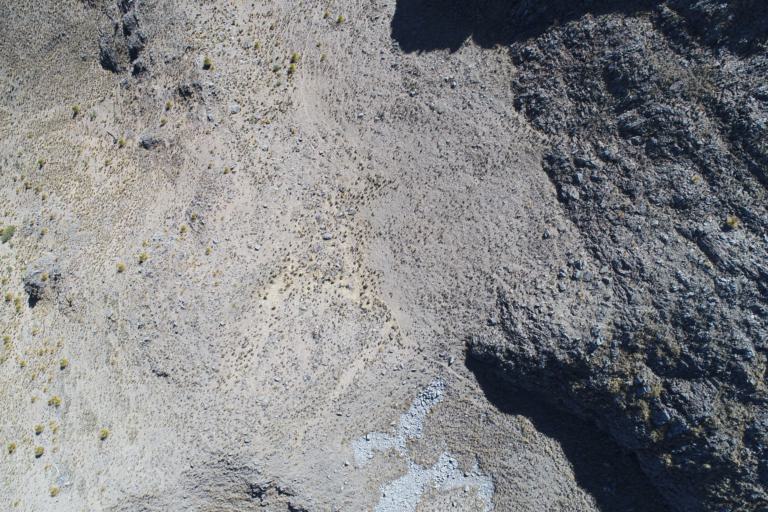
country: BO
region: La Paz
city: Viloco
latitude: -16.8066
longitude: -67.5455
